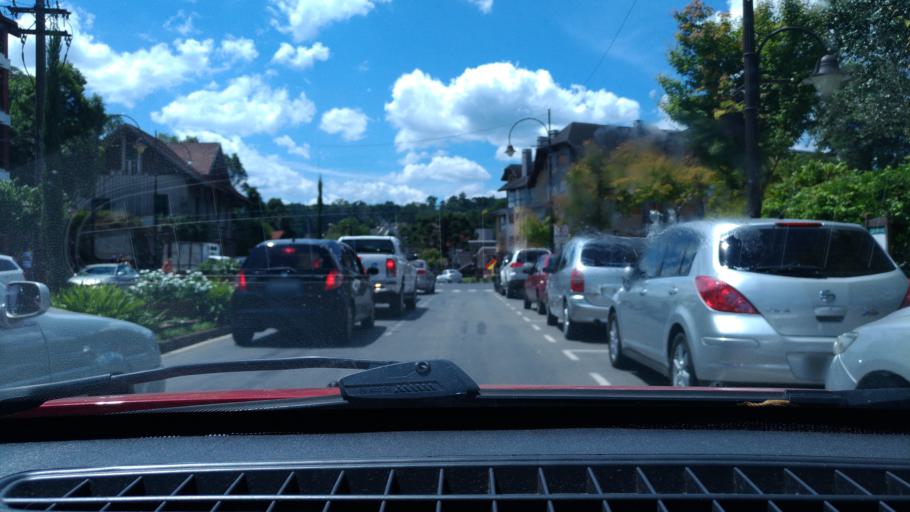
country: BR
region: Rio Grande do Sul
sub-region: Canela
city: Canela
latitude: -29.3829
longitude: -50.8721
